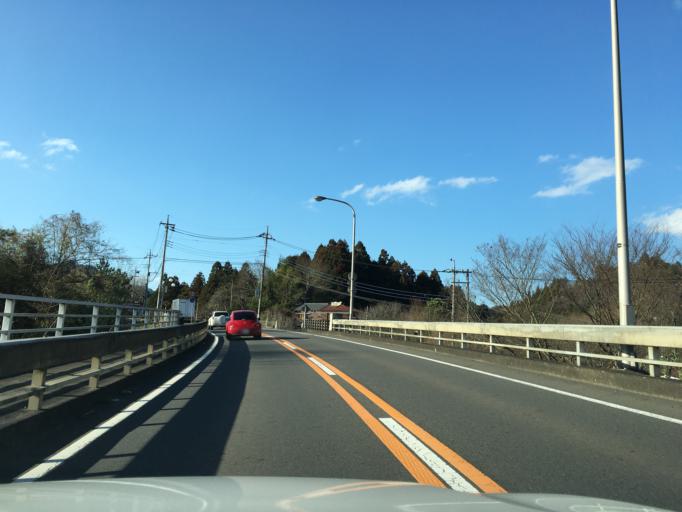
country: JP
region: Ibaraki
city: Daigo
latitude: 36.7143
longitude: 140.3869
